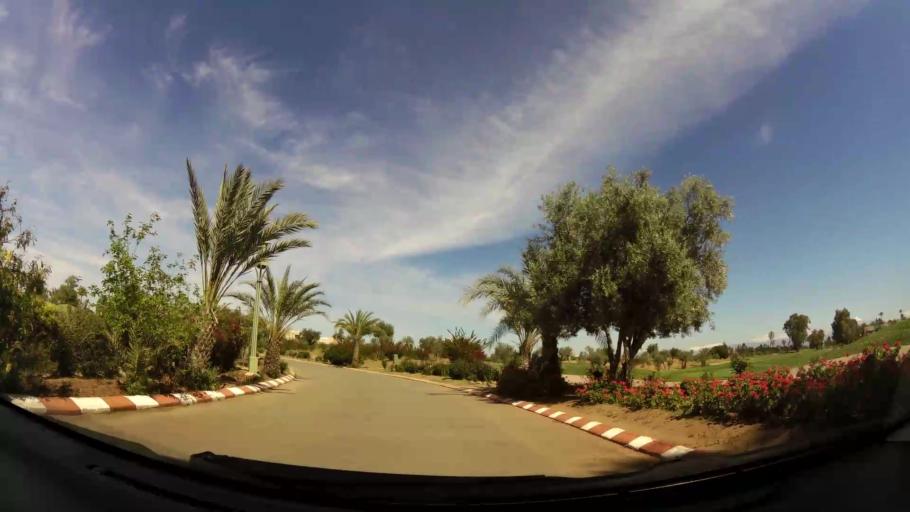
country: MA
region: Marrakech-Tensift-Al Haouz
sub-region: Marrakech
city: Marrakesh
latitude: 31.6124
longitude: -7.9351
